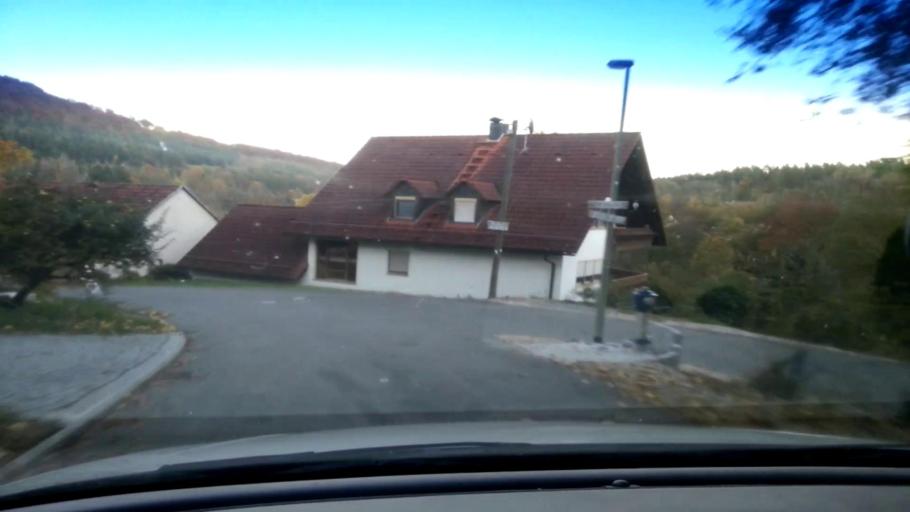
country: DE
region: Bavaria
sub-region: Upper Franconia
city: Heiligenstadt
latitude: 49.8751
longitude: 11.1355
